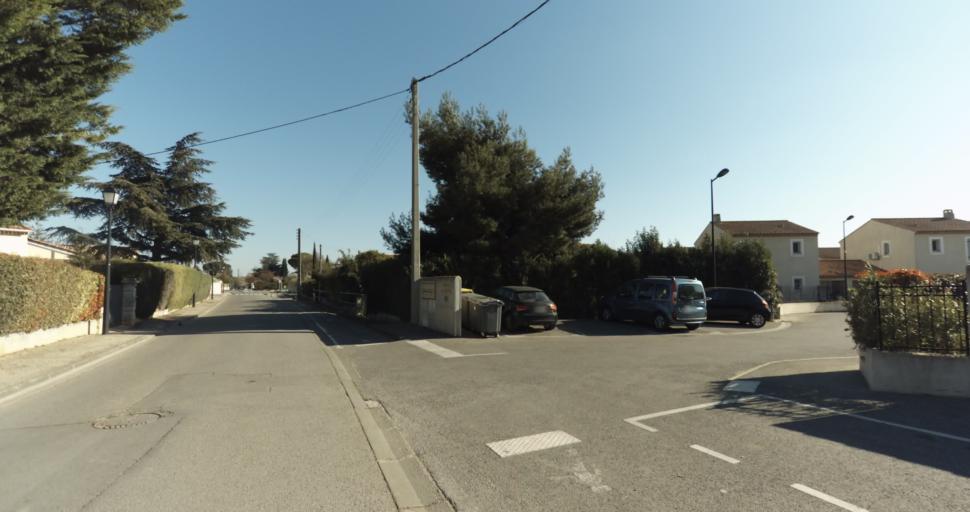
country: FR
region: Provence-Alpes-Cote d'Azur
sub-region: Departement des Bouches-du-Rhone
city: Pelissanne
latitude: 43.6357
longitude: 5.1431
